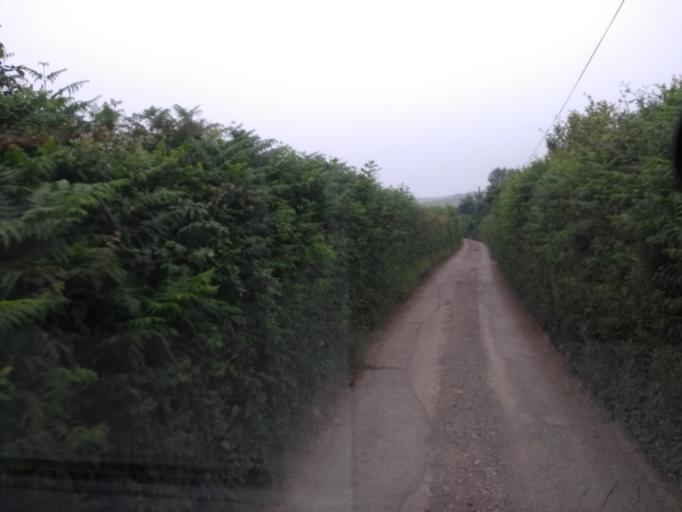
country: GB
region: England
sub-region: Dorset
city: Bridport
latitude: 50.7256
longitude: -2.7878
